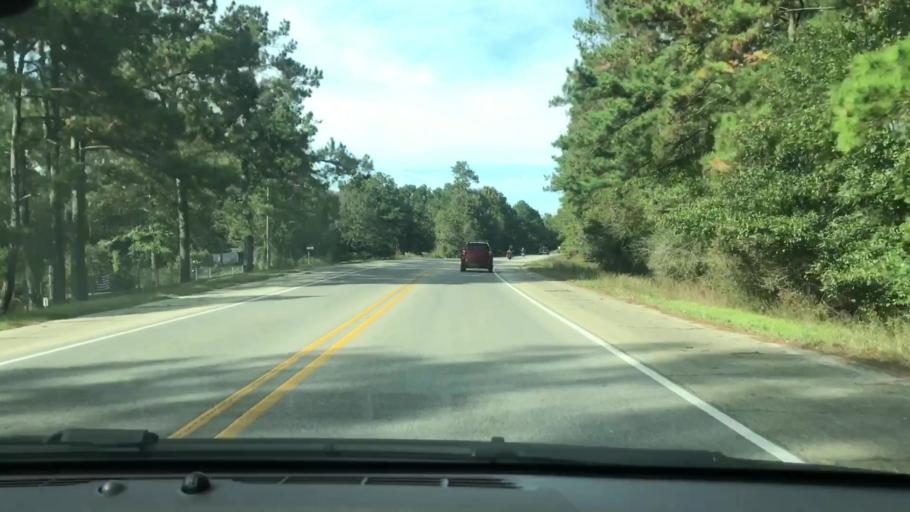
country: US
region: Louisiana
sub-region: Saint Tammany Parish
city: Pearl River
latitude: 30.4209
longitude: -89.7871
